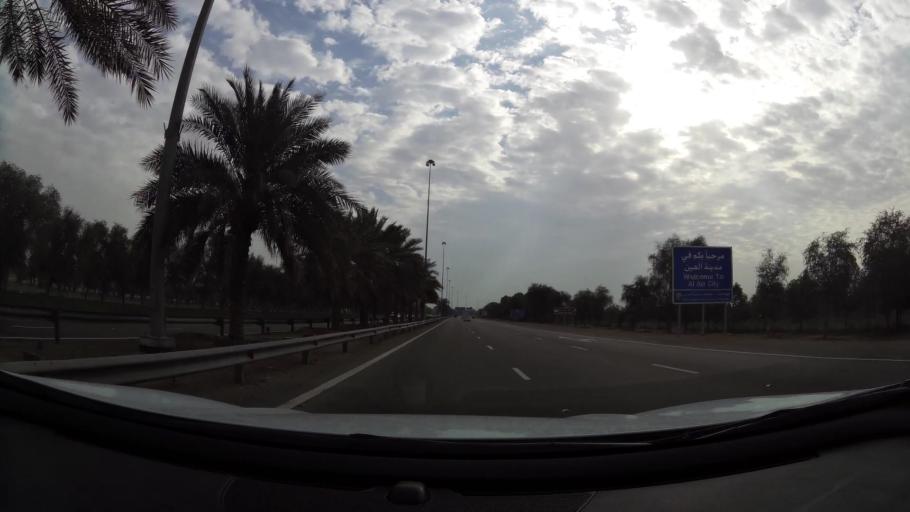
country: AE
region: Abu Dhabi
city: Al Ain
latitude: 24.2019
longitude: 55.5721
